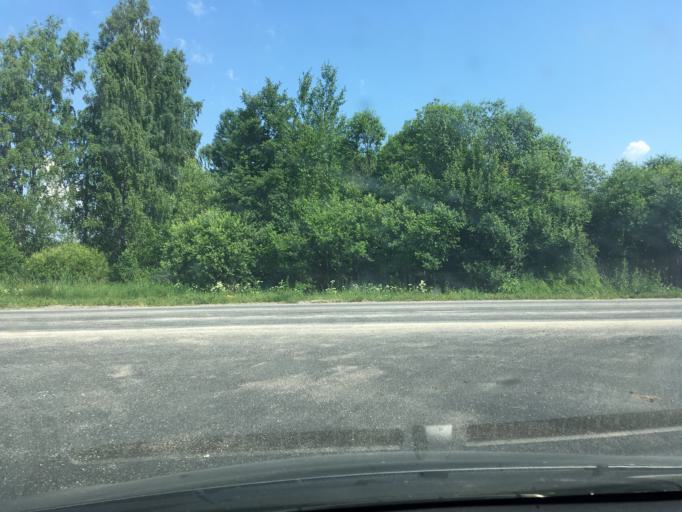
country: EE
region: Laeaene
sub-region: Lihula vald
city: Lihula
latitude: 58.6685
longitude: 23.7661
